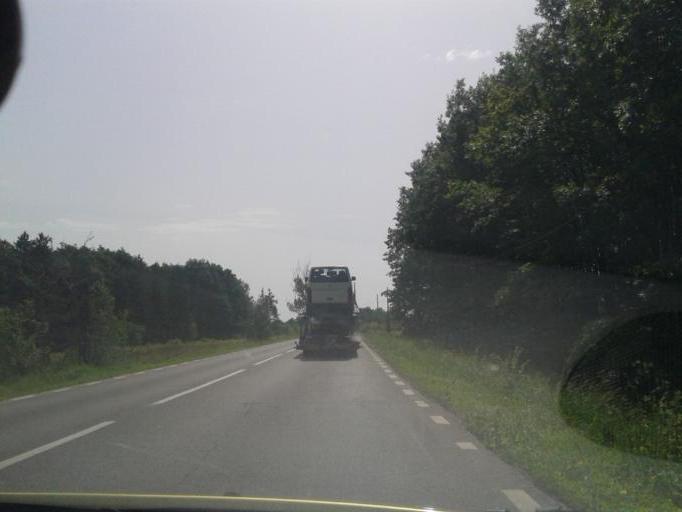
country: RO
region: Arges
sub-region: Comuna Cotmeana
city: Cotmeana
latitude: 44.9894
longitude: 24.6404
